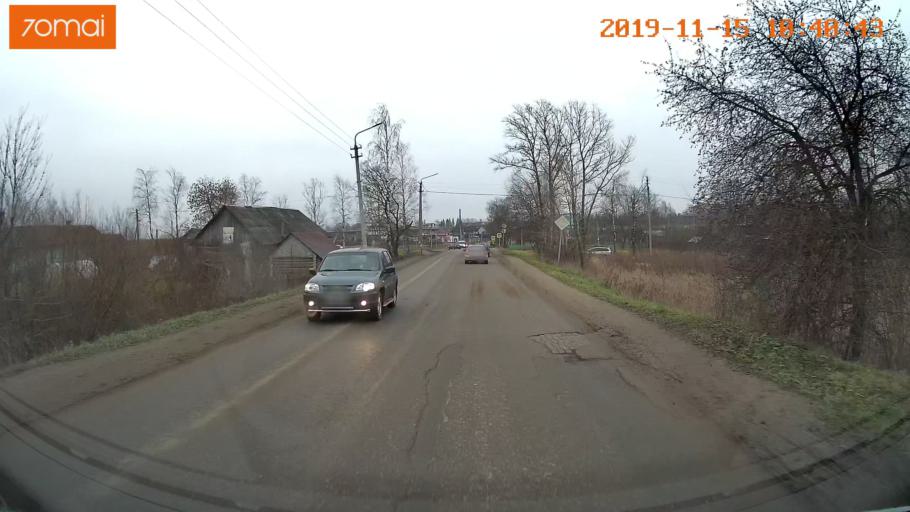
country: RU
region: Vologda
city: Sheksna
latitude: 59.2126
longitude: 38.5103
